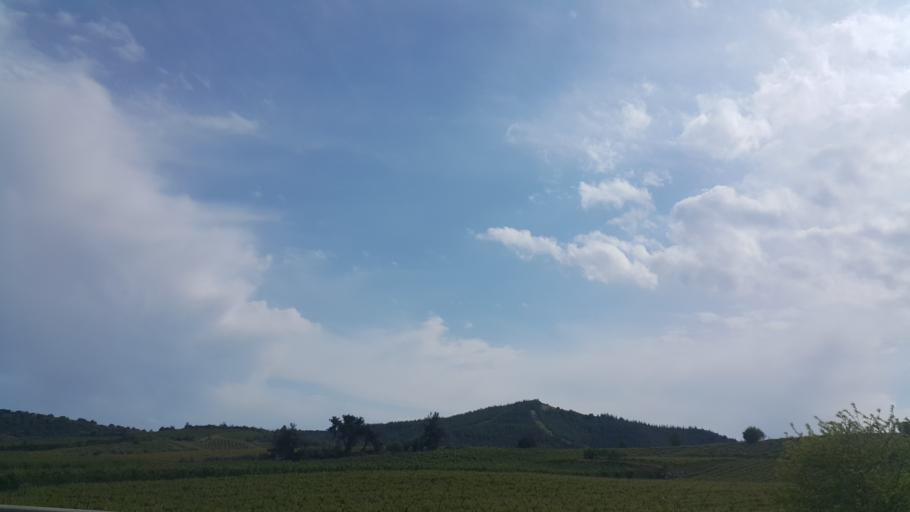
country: TR
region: Mersin
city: Tarsus
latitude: 36.9546
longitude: 34.7618
